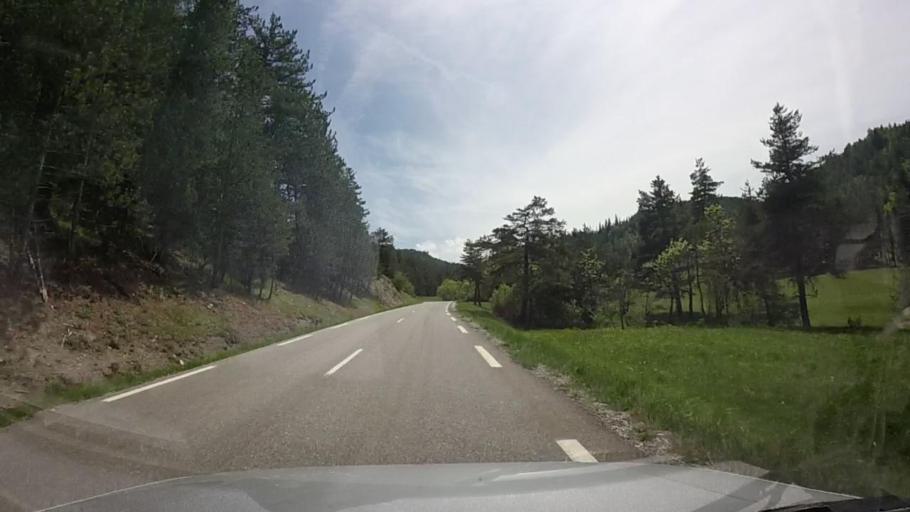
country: FR
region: Provence-Alpes-Cote d'Azur
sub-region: Departement des Alpes-de-Haute-Provence
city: Seyne-les-Alpes
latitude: 44.2565
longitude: 6.3659
